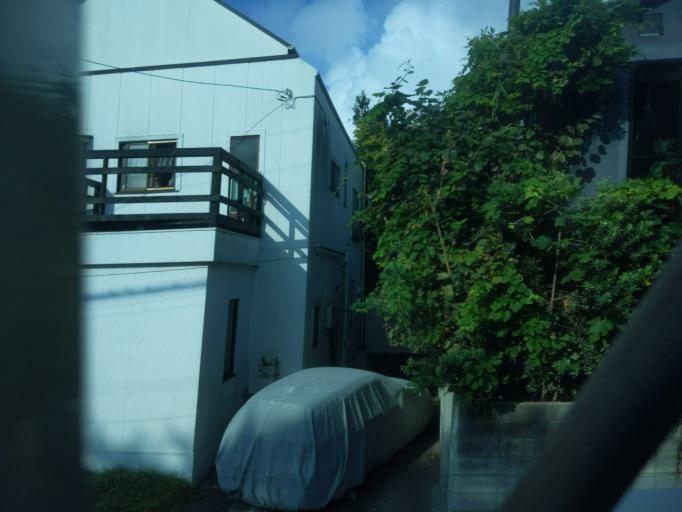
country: JP
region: Tokyo
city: Musashino
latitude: 35.6951
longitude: 139.5857
